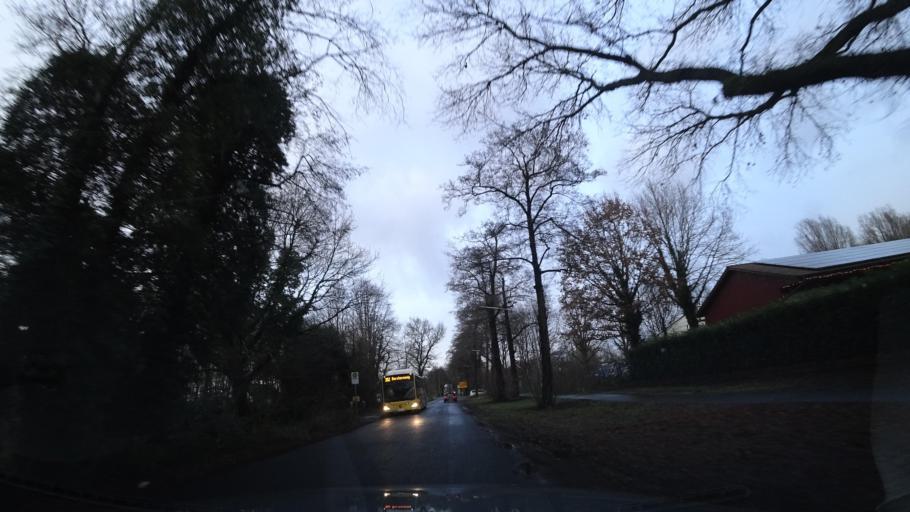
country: DE
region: Lower Saxony
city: Oldenburg
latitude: 53.1035
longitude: 8.2761
